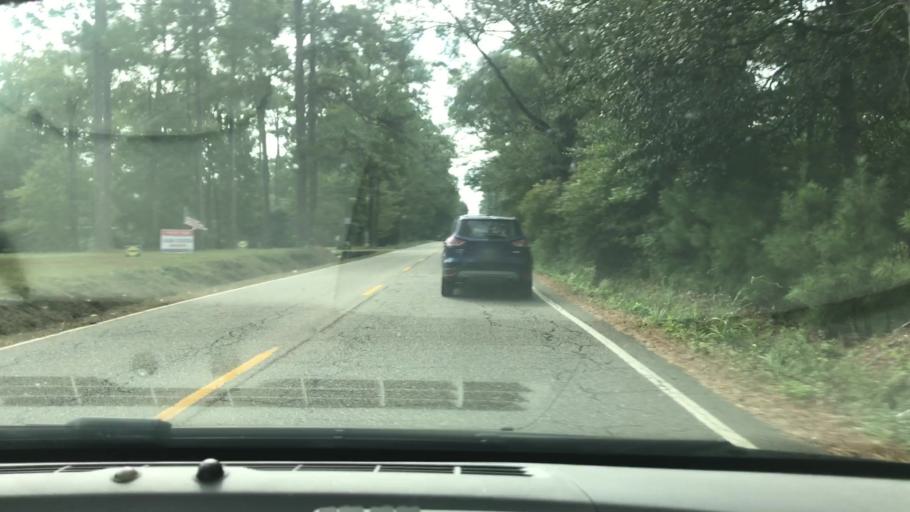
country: US
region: Louisiana
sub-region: Saint Tammany Parish
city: Abita Springs
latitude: 30.4740
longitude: -90.0408
